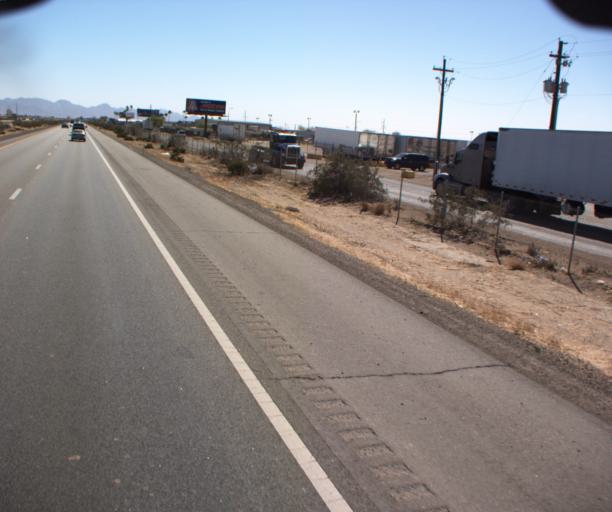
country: US
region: Arizona
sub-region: Yuma County
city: Yuma
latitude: 32.6833
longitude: -114.5603
